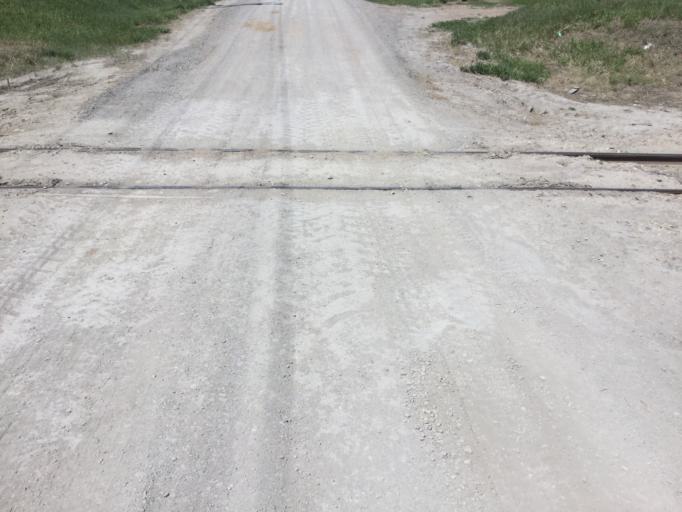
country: US
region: Kansas
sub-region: Phillips County
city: Phillipsburg
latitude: 39.7714
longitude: -99.3471
